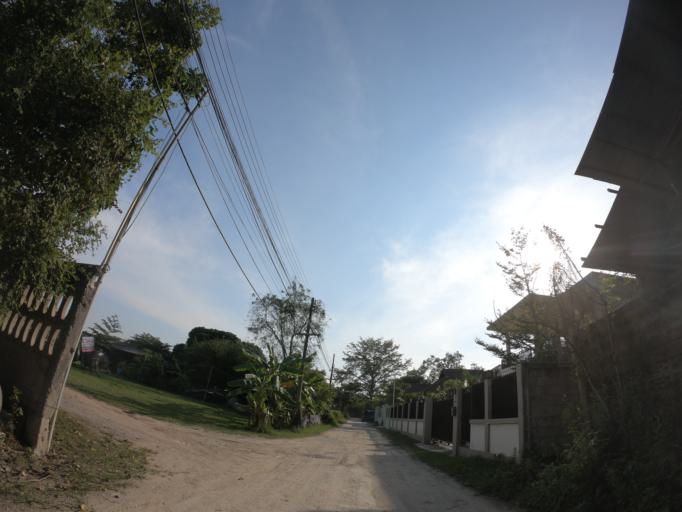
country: TH
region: Chiang Mai
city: Chiang Mai
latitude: 18.8267
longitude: 98.9860
